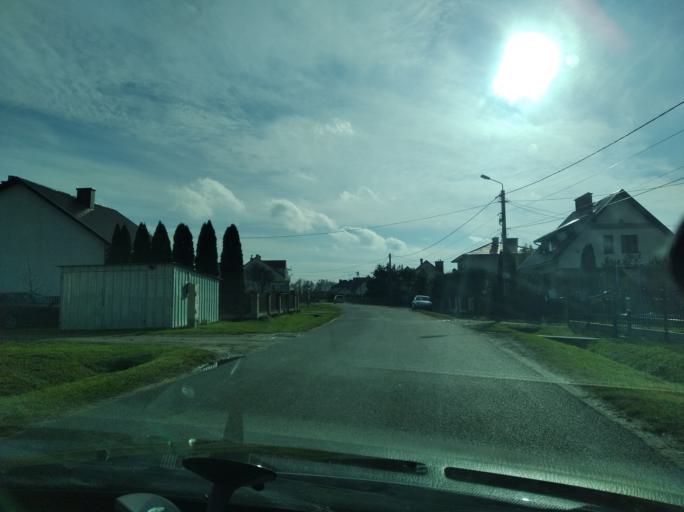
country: PL
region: Subcarpathian Voivodeship
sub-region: Powiat ropczycko-sedziszowski
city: Sedziszow Malopolski
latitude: 50.1048
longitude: 21.7330
